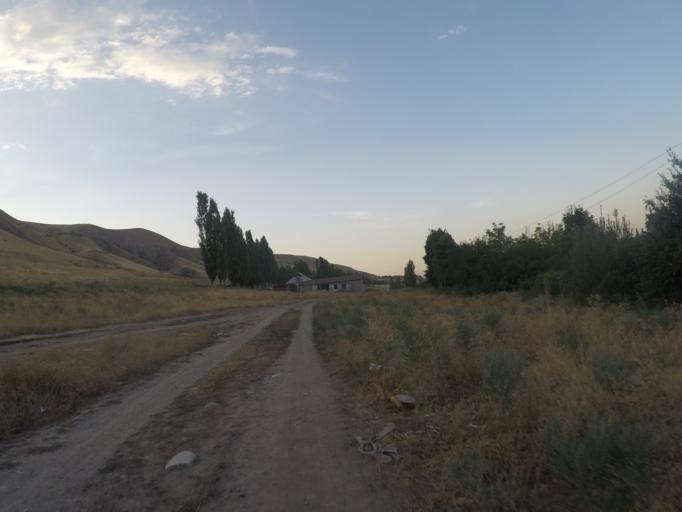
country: KG
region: Chuy
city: Bishkek
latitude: 42.7715
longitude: 74.6396
